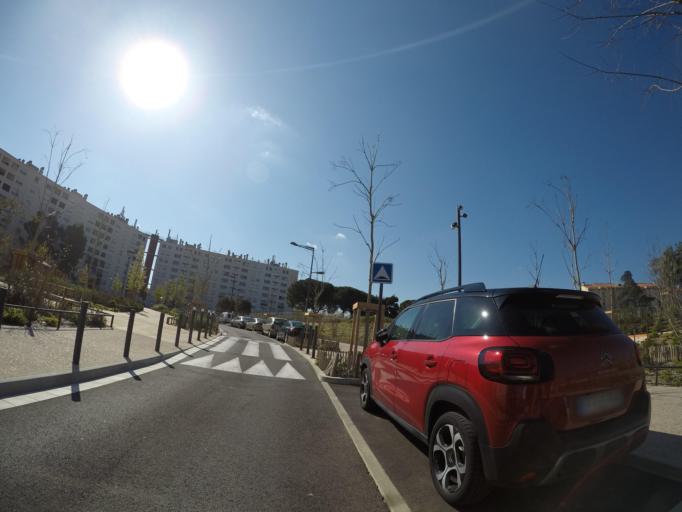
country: FR
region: Languedoc-Roussillon
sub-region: Departement des Pyrenees-Orientales
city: Perpignan
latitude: 42.6945
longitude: 2.9068
